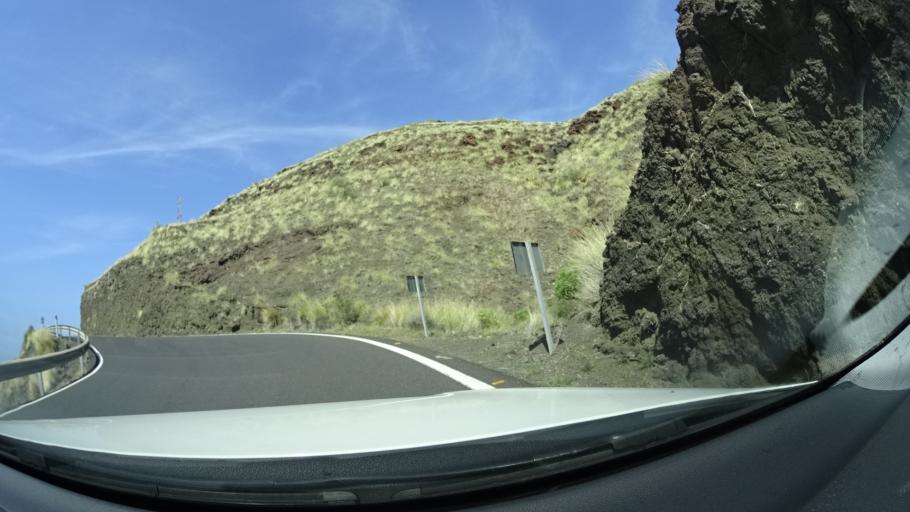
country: ES
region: Canary Islands
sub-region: Provincia de Las Palmas
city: Agaete
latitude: 28.0848
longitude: -15.7034
